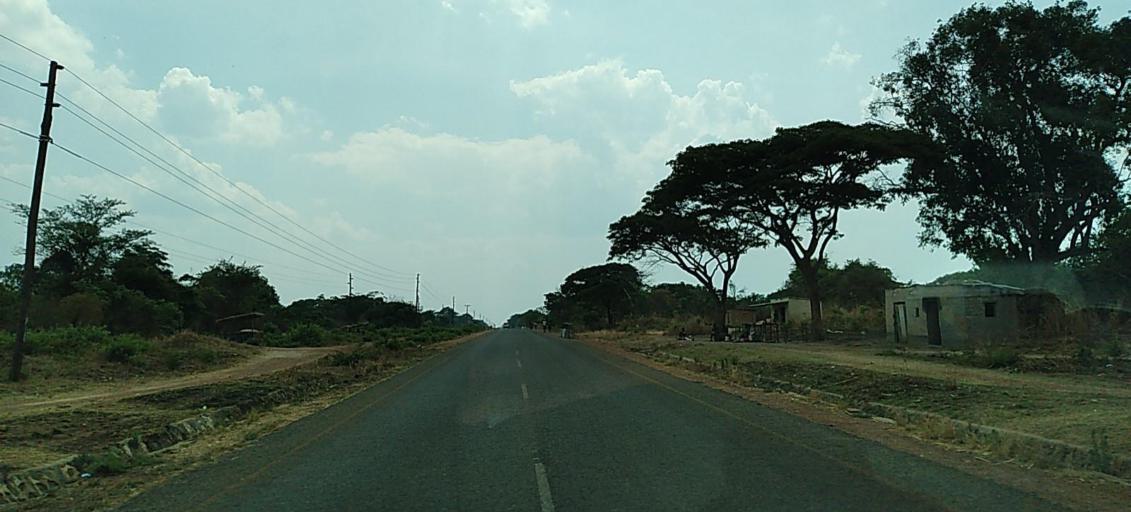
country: ZM
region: Copperbelt
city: Chingola
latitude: -12.8566
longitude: 27.6453
